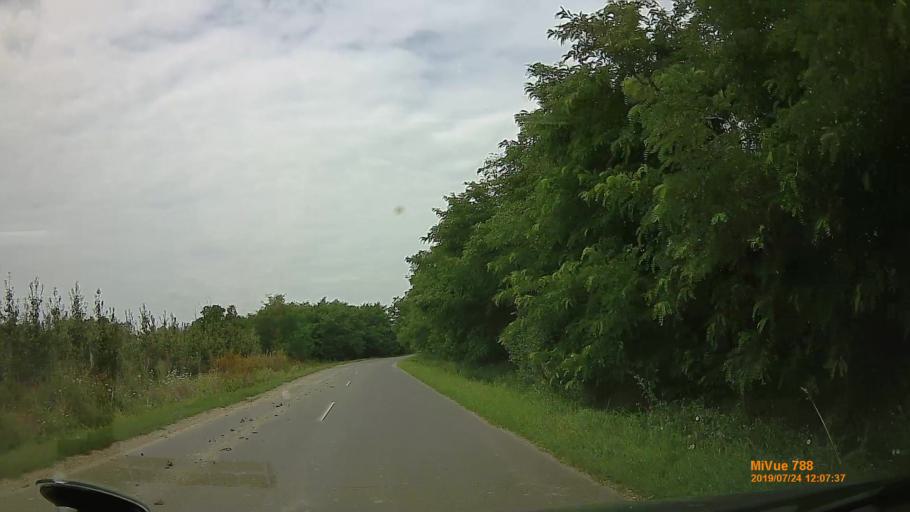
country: HU
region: Szabolcs-Szatmar-Bereg
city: Vasarosnameny
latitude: 48.1926
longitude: 22.3920
